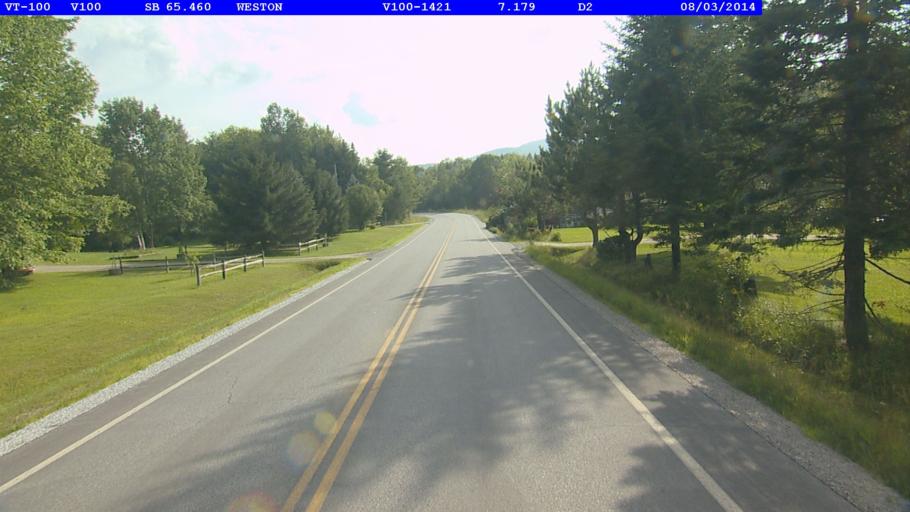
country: US
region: Vermont
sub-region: Windsor County
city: Chester
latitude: 43.3441
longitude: -72.7797
